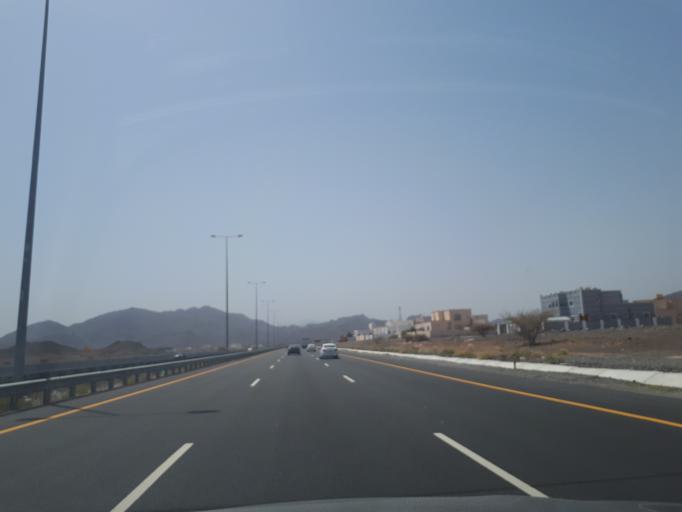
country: OM
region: Muhafazat ad Dakhiliyah
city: Bidbid
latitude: 23.3388
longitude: 58.1096
